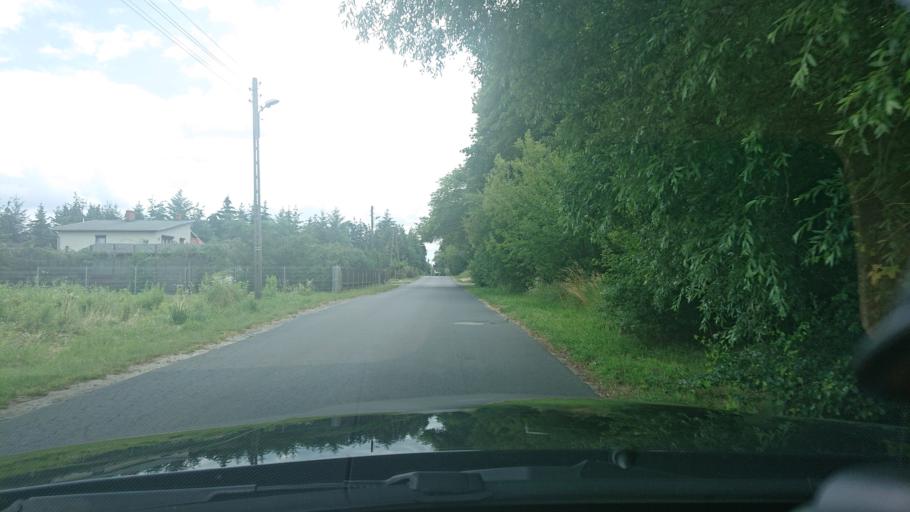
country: PL
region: Greater Poland Voivodeship
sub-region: Powiat gnieznienski
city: Gniezno
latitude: 52.5187
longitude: 17.6174
